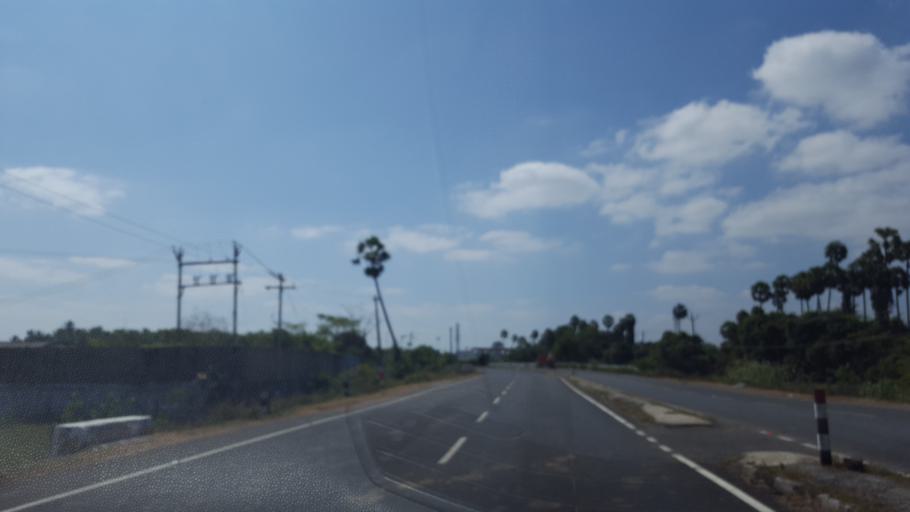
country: IN
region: Tamil Nadu
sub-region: Kancheepuram
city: Mamallapuram
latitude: 12.6200
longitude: 80.1696
